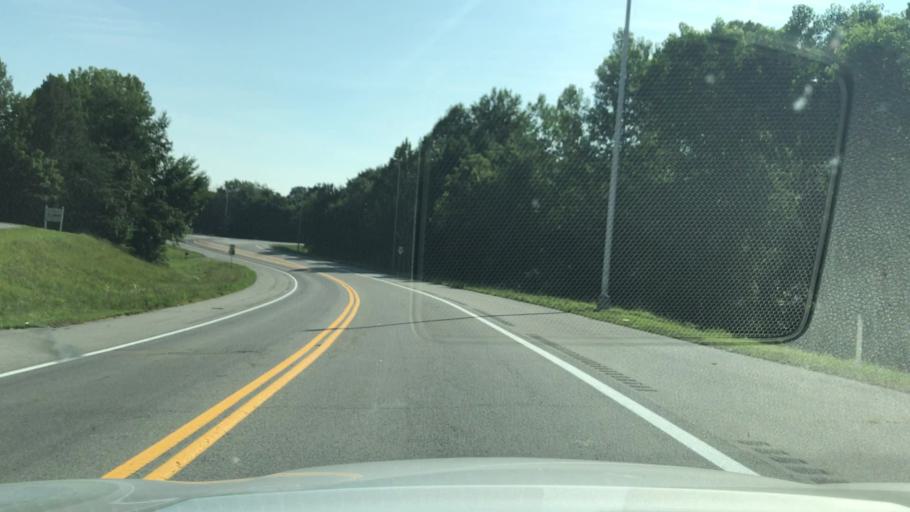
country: US
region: Tennessee
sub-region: Pickett County
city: Byrdstown
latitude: 36.5838
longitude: -85.1294
